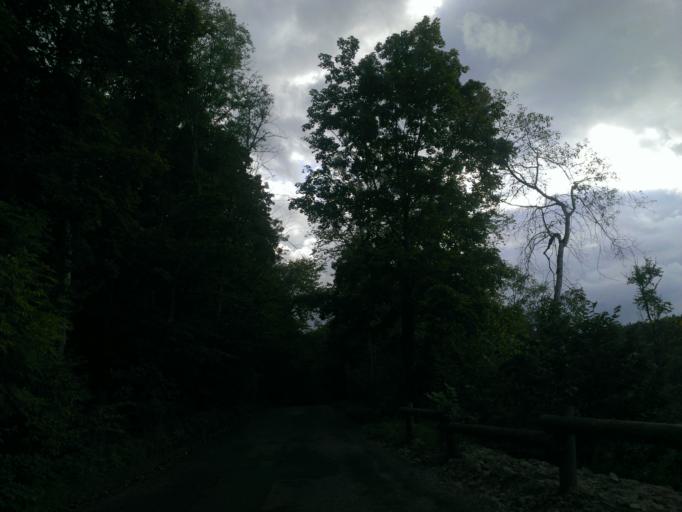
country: LV
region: Sigulda
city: Sigulda
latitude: 57.1634
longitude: 24.8400
